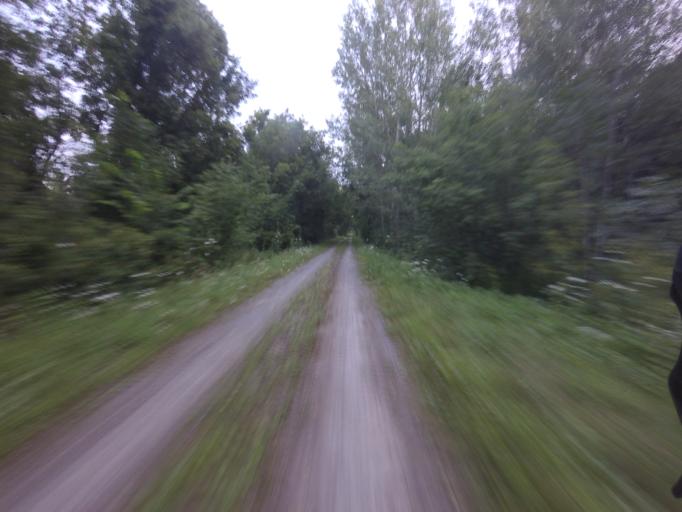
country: CA
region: Ontario
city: Carleton Place
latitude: 45.1651
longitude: -76.0699
